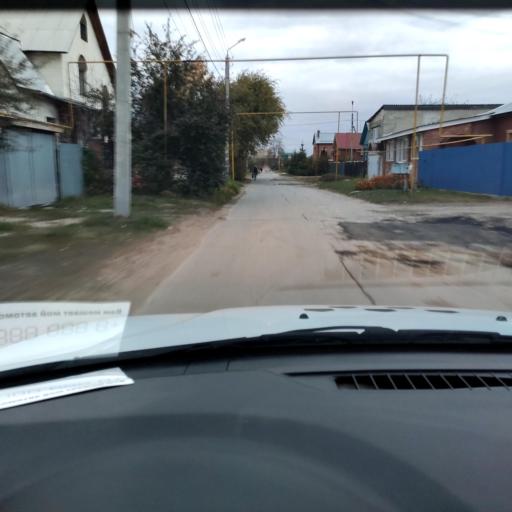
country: RU
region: Samara
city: Tol'yatti
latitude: 53.5241
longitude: 49.4254
